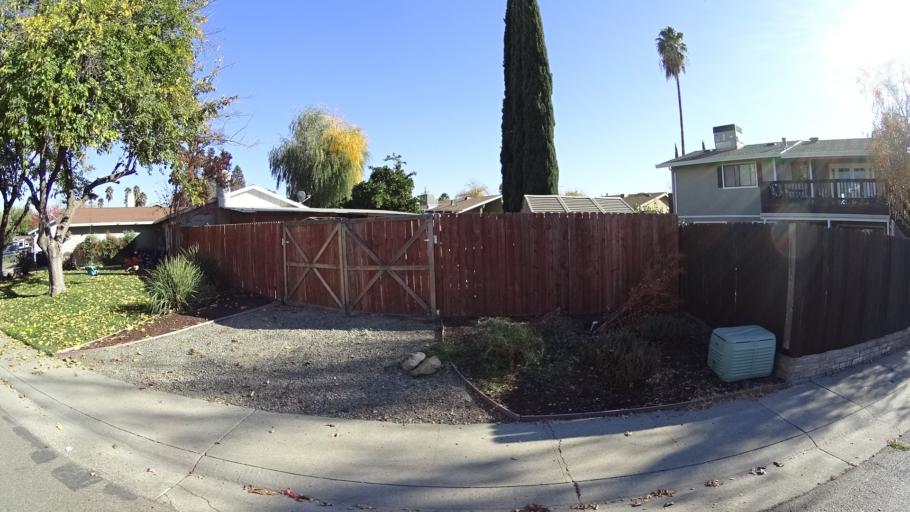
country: US
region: California
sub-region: Sacramento County
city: Antelope
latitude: 38.7138
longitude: -121.3169
